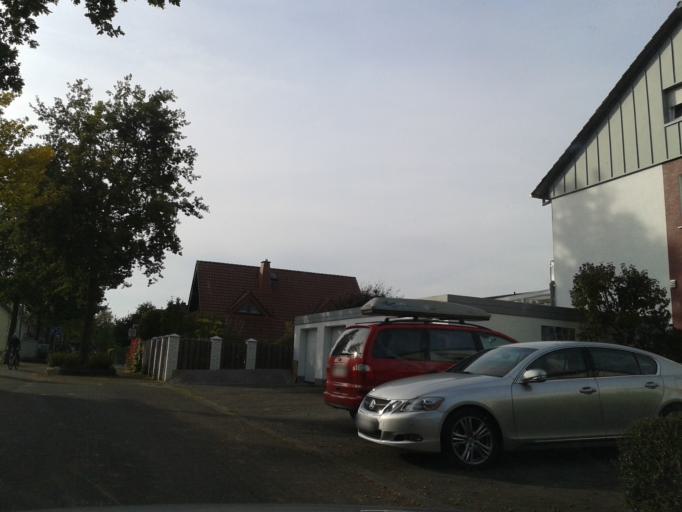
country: DE
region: North Rhine-Westphalia
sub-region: Regierungsbezirk Detmold
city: Paderborn
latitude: 51.7276
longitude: 8.6860
